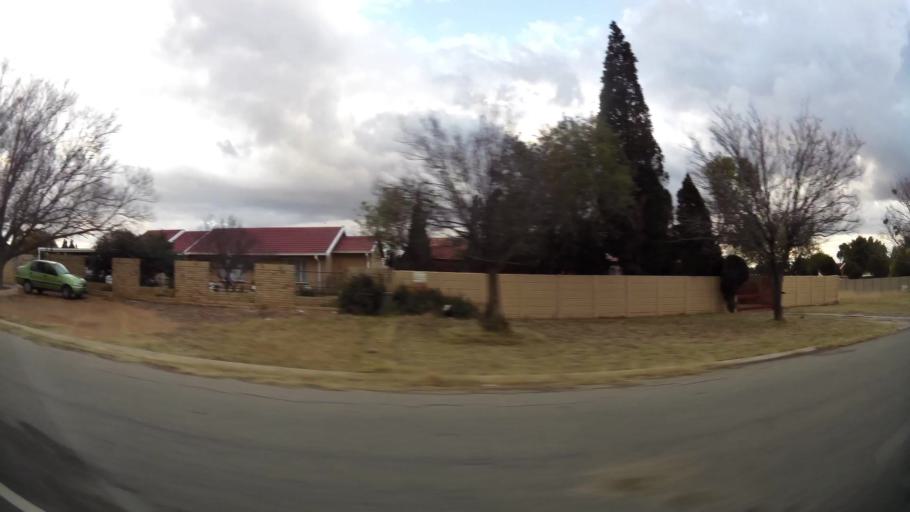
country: ZA
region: Orange Free State
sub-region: Lejweleputswa District Municipality
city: Welkom
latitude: -27.9440
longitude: 26.7252
